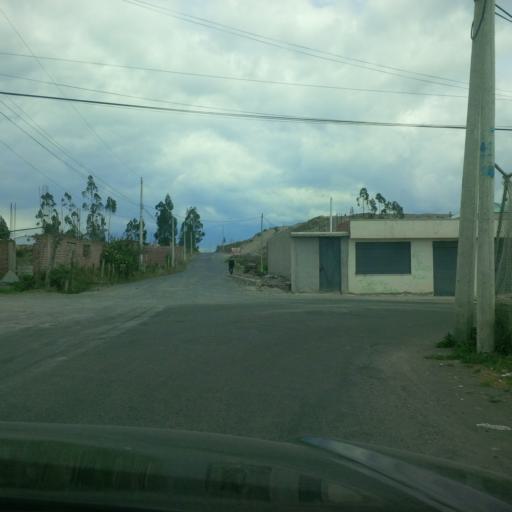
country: EC
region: Chimborazo
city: Riobamba
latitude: -1.6418
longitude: -78.6525
